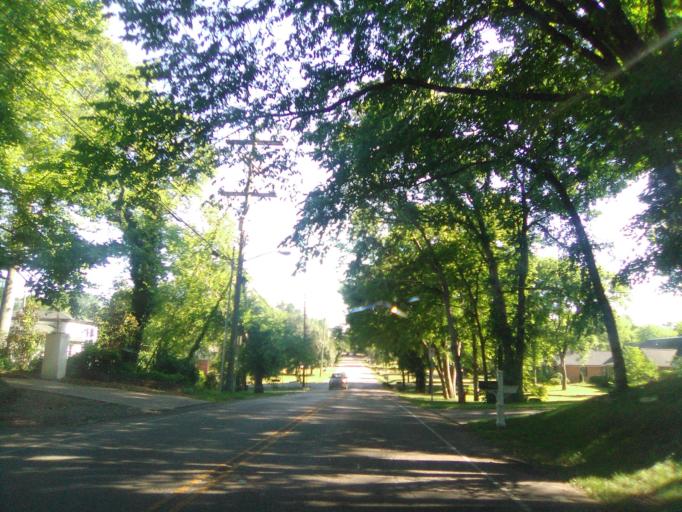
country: US
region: Tennessee
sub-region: Davidson County
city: Belle Meade
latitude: 36.1197
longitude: -86.8359
